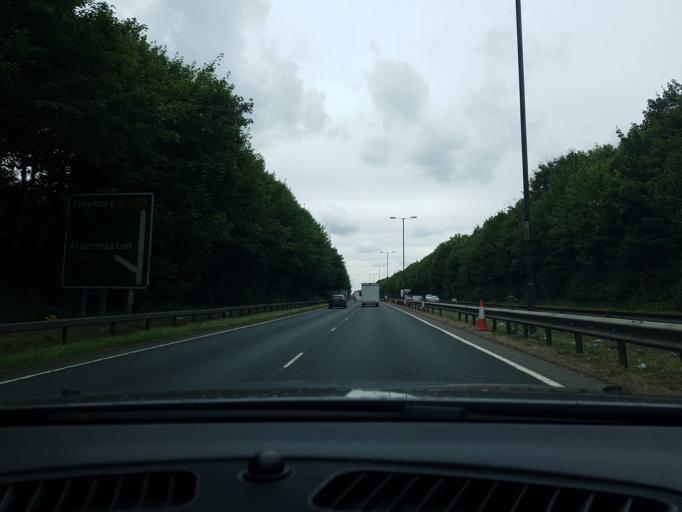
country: GB
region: England
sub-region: Hampshire
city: Basingstoke
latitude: 51.2790
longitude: -1.0894
